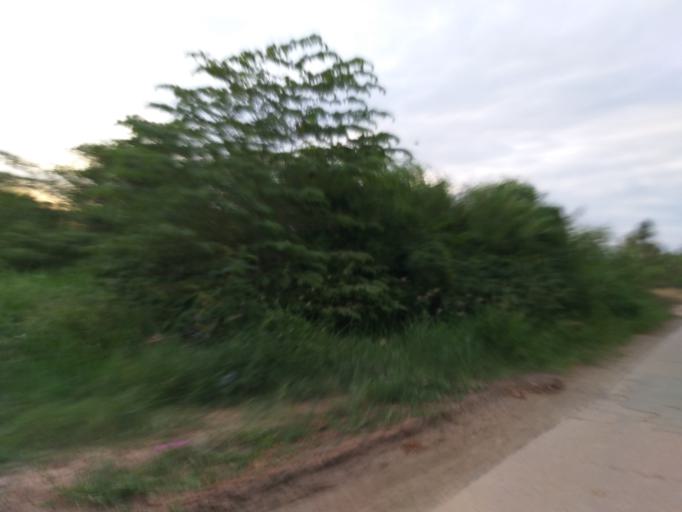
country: TH
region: Pathum Thani
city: Ban Lam Luk Ka
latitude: 14.0028
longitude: 100.8002
